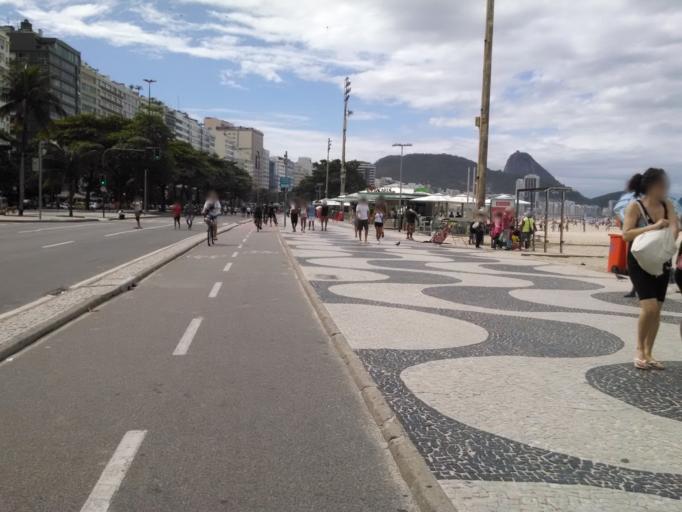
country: BR
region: Rio de Janeiro
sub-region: Rio De Janeiro
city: Rio de Janeiro
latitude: -22.9765
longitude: -43.1879
